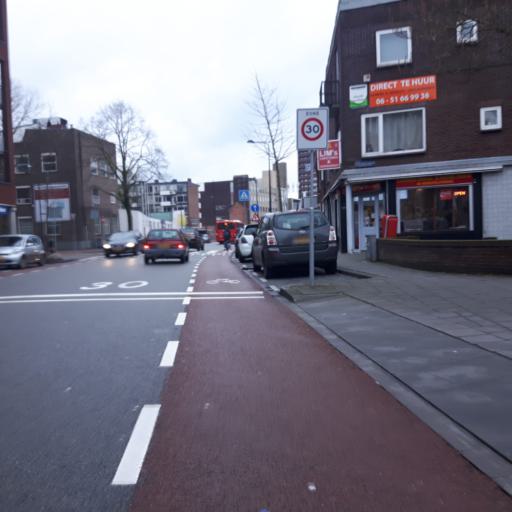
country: NL
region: Overijssel
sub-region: Gemeente Enschede
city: Enschede
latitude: 52.2152
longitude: 6.8963
